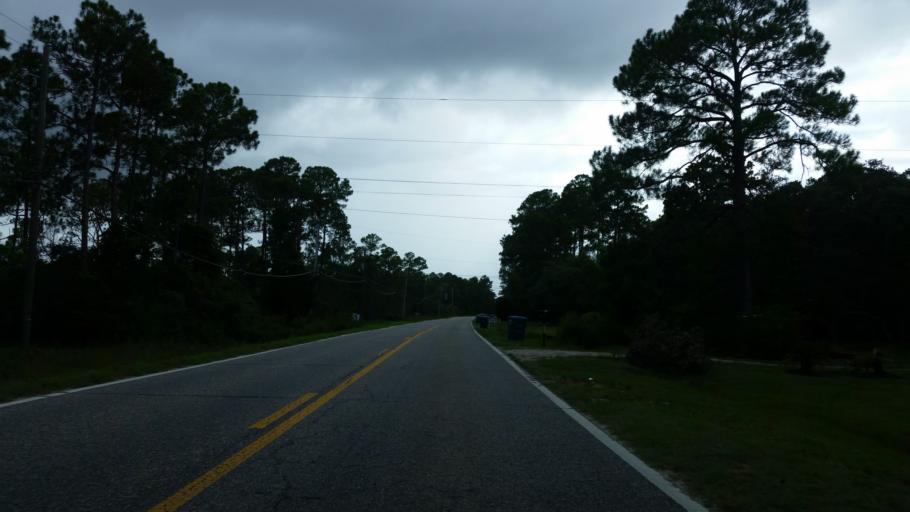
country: US
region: Florida
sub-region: Santa Rosa County
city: Holley
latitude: 30.4353
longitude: -86.9585
